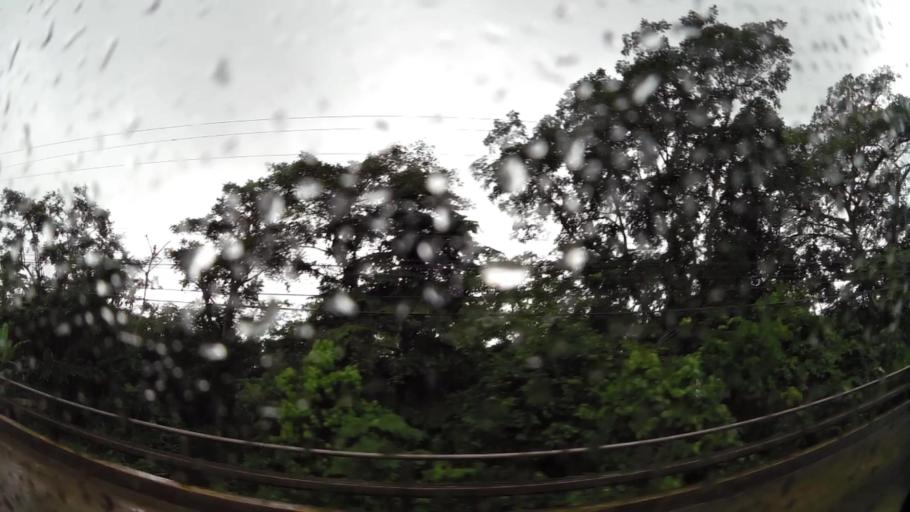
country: PA
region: Colon
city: Buena Vista
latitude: 9.2753
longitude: -79.6981
